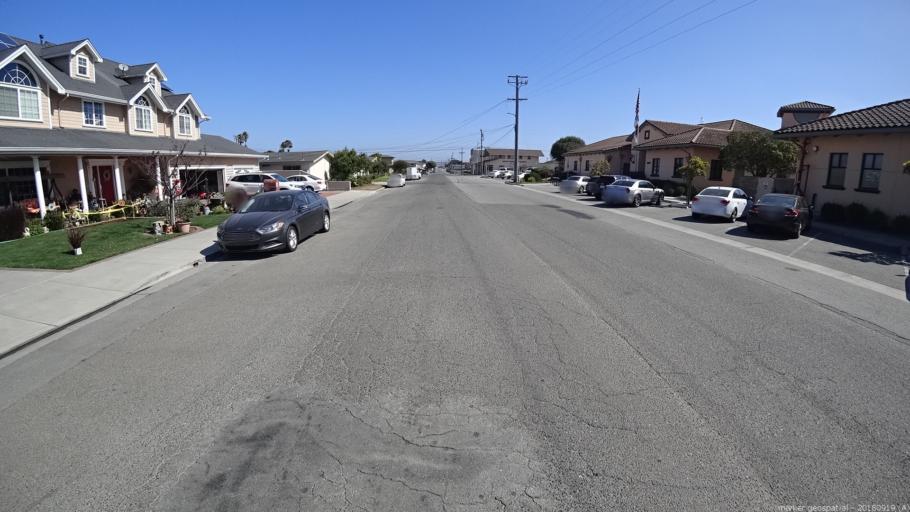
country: US
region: California
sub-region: Monterey County
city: Castroville
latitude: 36.7675
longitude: -121.7582
